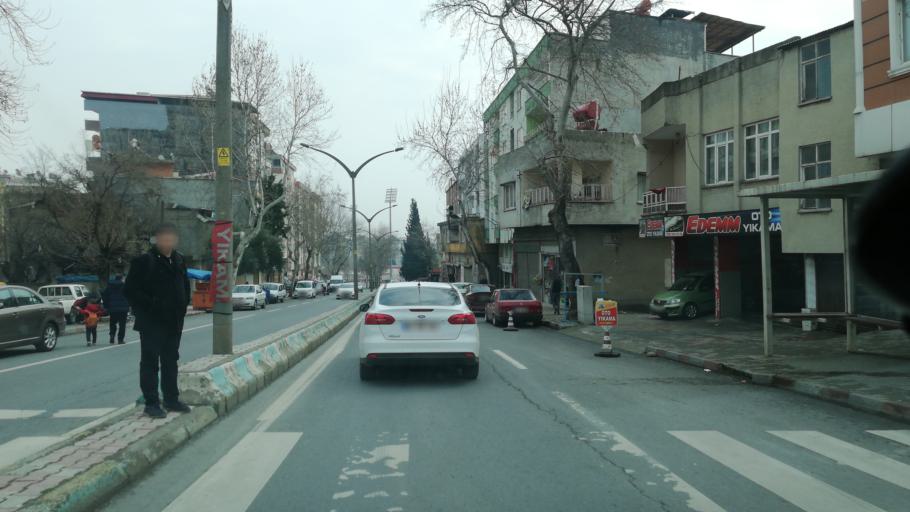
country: TR
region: Kahramanmaras
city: Kahramanmaras
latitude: 37.5766
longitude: 36.9198
